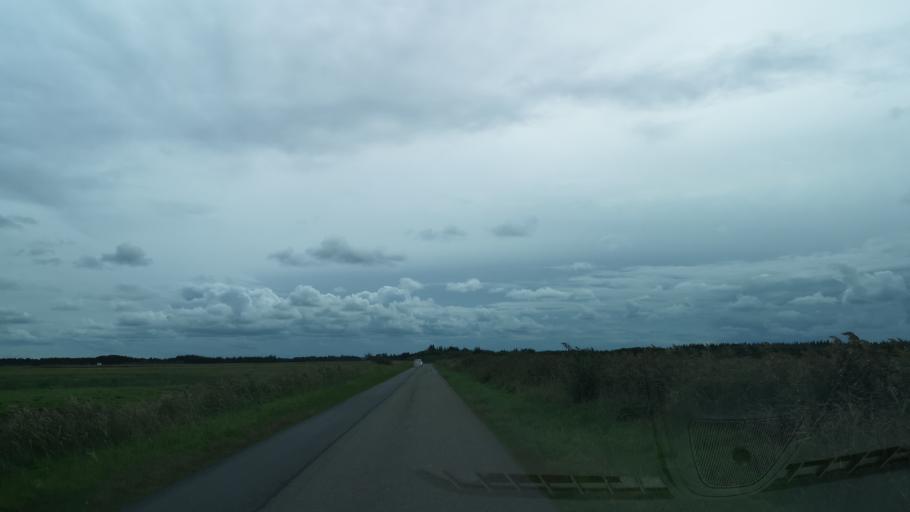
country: DK
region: Central Jutland
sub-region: Ringkobing-Skjern Kommune
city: Hvide Sande
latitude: 55.8374
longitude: 8.2176
